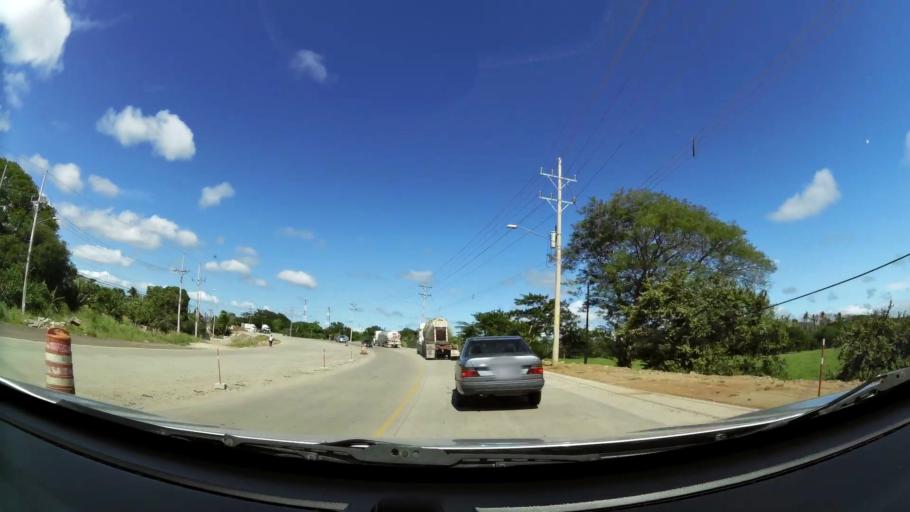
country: CR
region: Guanacaste
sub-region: Canton de Canas
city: Canas
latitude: 10.4198
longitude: -85.0875
